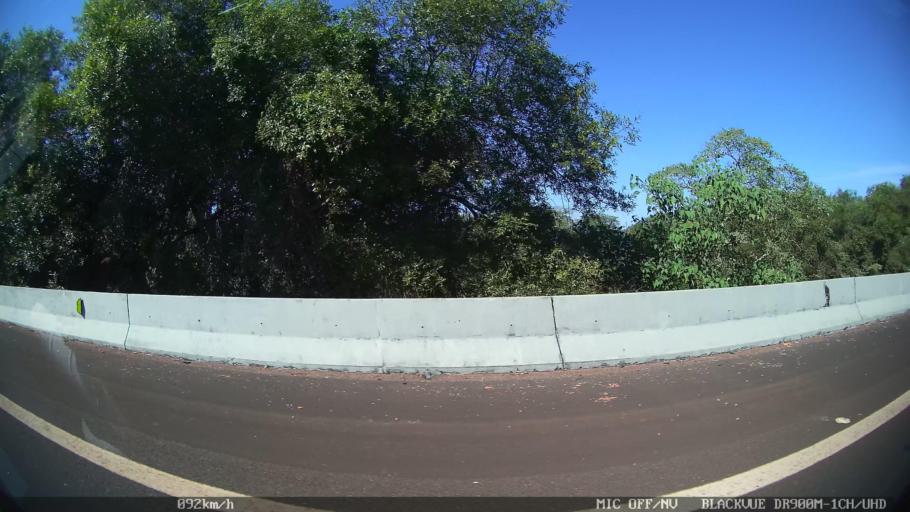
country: BR
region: Sao Paulo
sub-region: Batatais
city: Batatais
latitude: -20.7302
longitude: -47.5226
